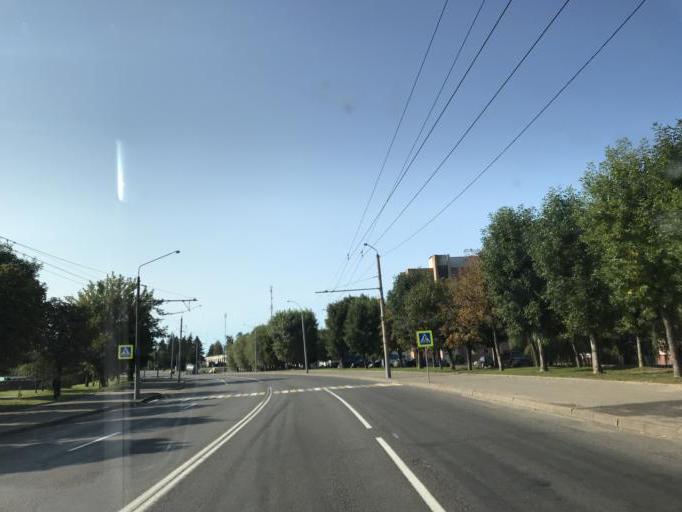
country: BY
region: Mogilev
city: Buynichy
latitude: 53.8812
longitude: 30.2678
